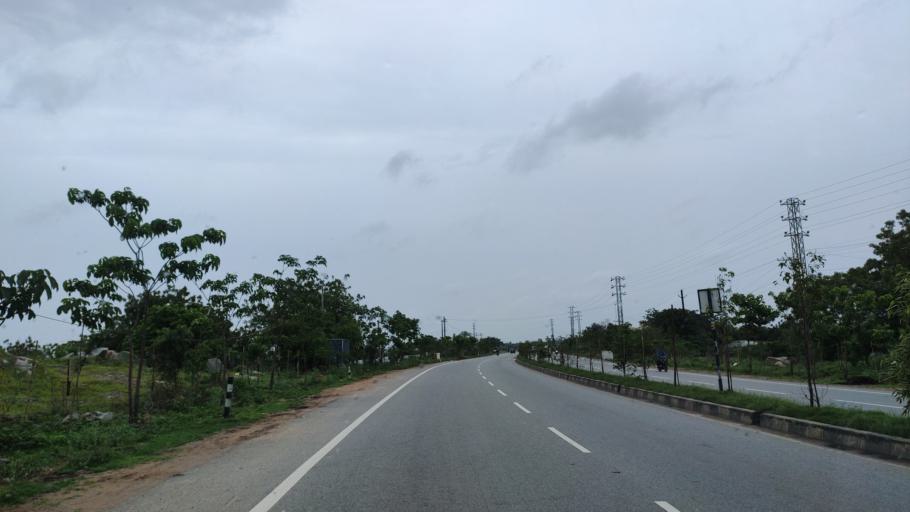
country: IN
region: Telangana
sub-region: Rangareddi
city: Secunderabad
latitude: 17.6030
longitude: 78.5677
